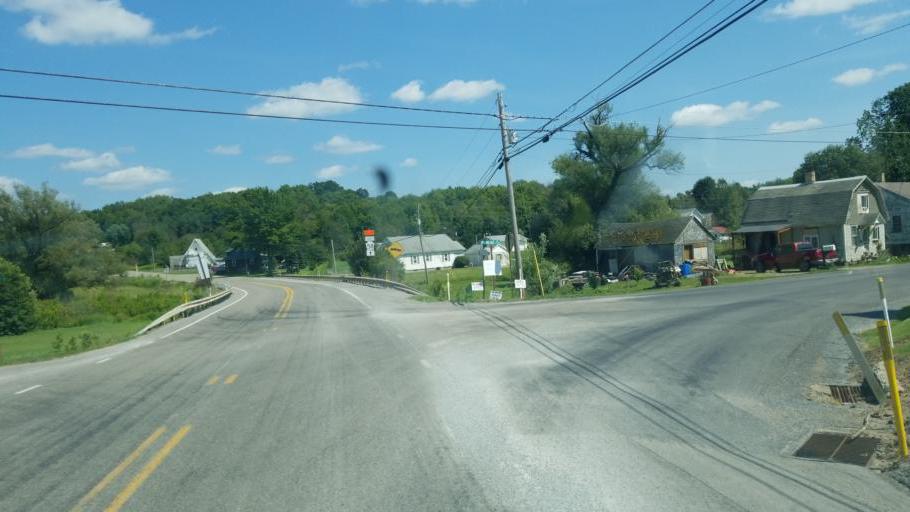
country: US
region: Pennsylvania
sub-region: Clarion County
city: Knox
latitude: 41.1073
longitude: -79.6247
